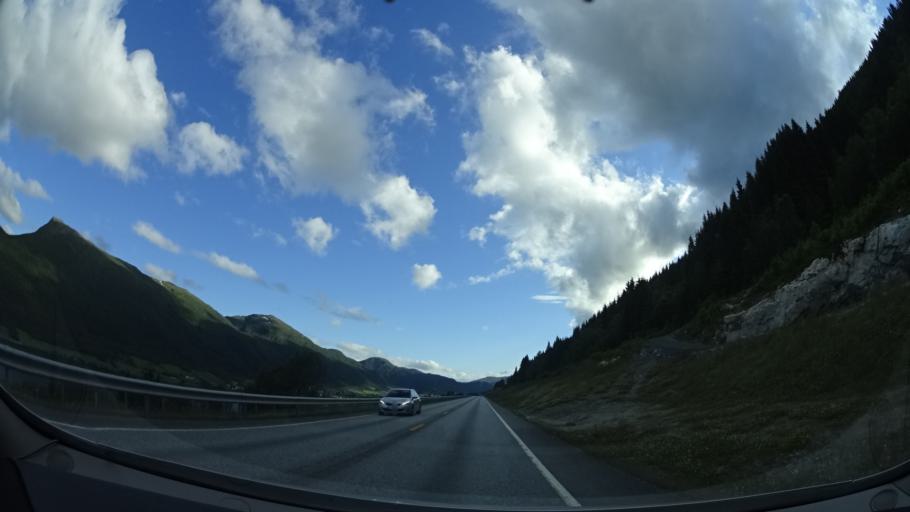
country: NO
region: More og Romsdal
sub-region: Gjemnes
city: Batnfjordsora
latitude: 62.9167
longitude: 7.6936
